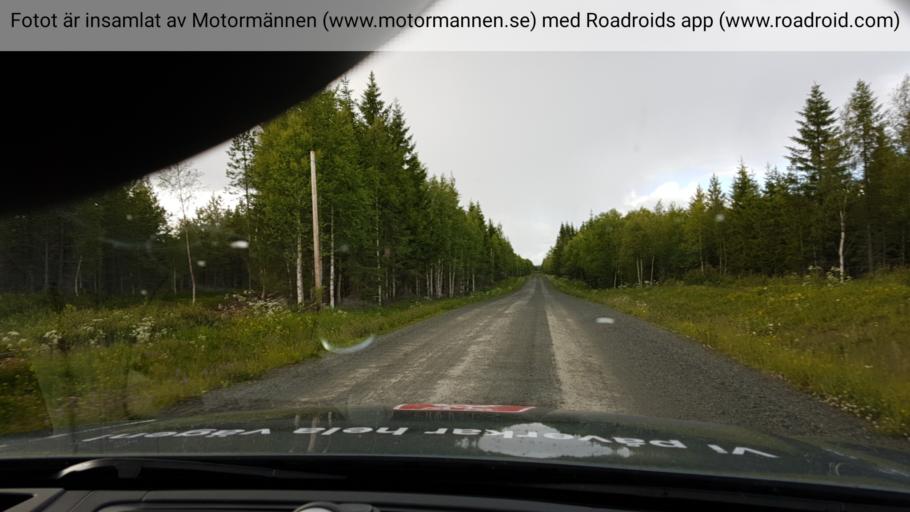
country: SE
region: Jaemtland
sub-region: Bergs Kommun
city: Hoverberg
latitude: 62.9703
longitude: 14.2213
